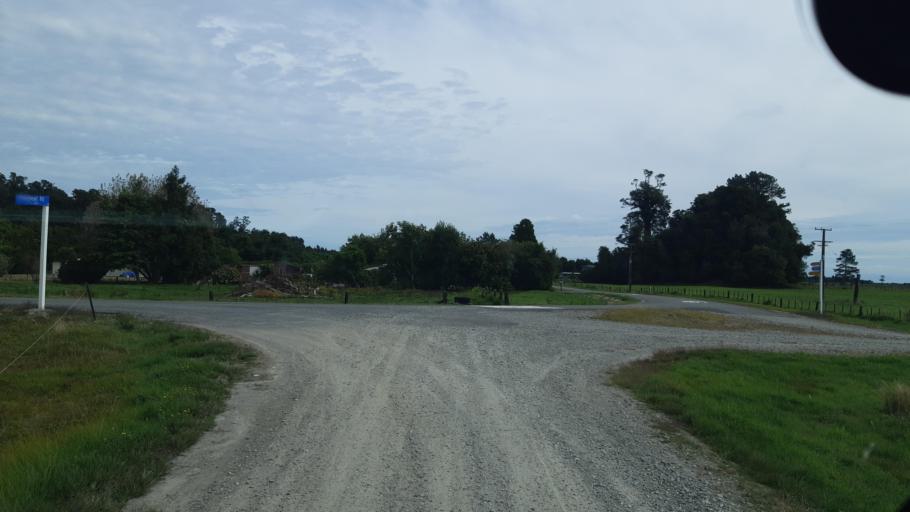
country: NZ
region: West Coast
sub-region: Westland District
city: Hokitika
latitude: -42.9751
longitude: 170.6853
